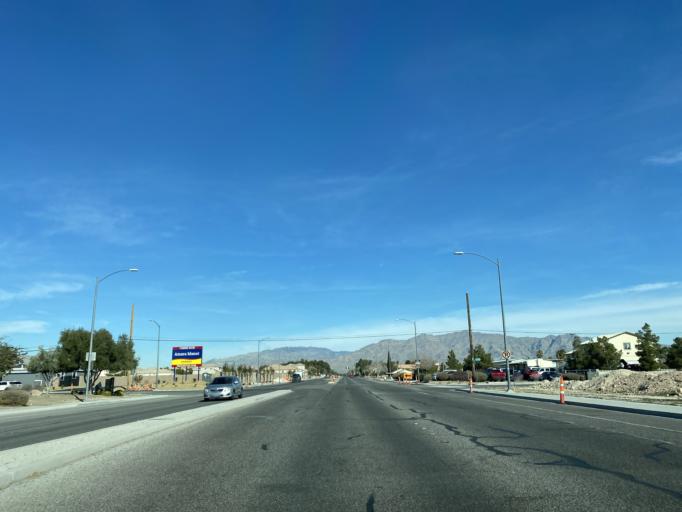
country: US
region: Nevada
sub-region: Clark County
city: Las Vegas
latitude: 36.2495
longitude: -115.2255
